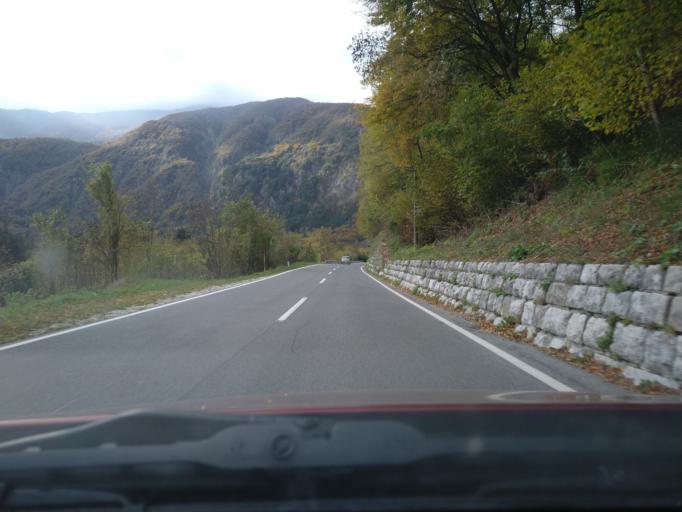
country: SI
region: Bovec
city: Bovec
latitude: 46.3122
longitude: 13.4844
